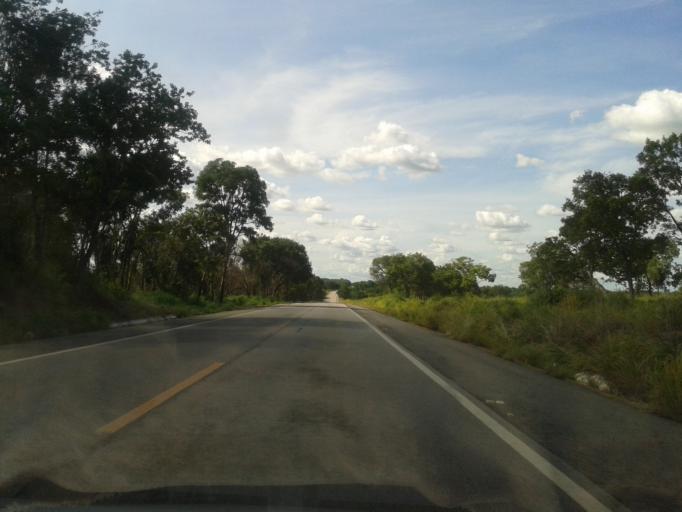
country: BR
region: Goias
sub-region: Mozarlandia
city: Mozarlandia
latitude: -15.2230
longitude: -50.5263
